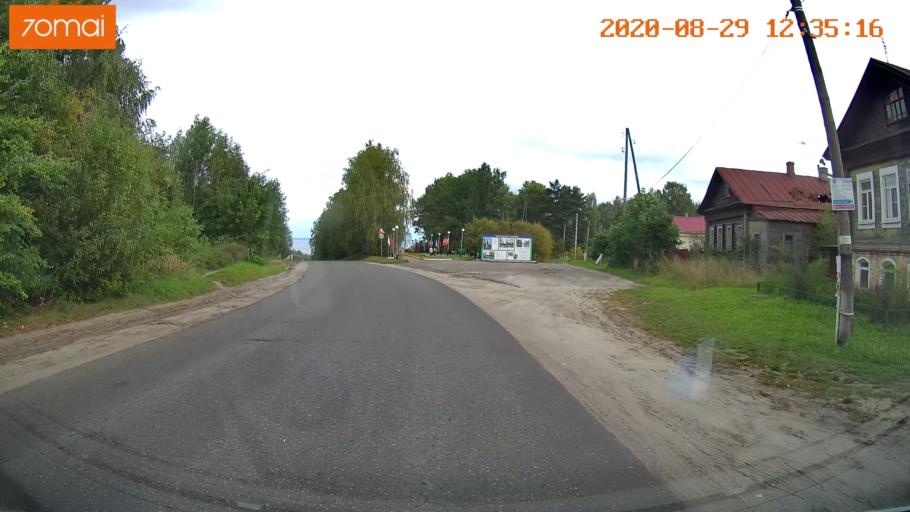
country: RU
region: Ivanovo
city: Yur'yevets
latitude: 57.3128
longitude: 43.1064
